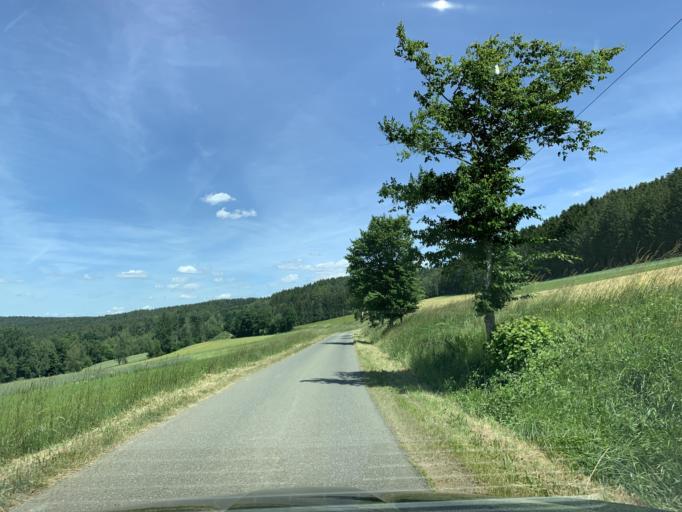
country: DE
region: Bavaria
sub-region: Upper Palatinate
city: Dieterskirchen
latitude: 49.4137
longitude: 12.4314
